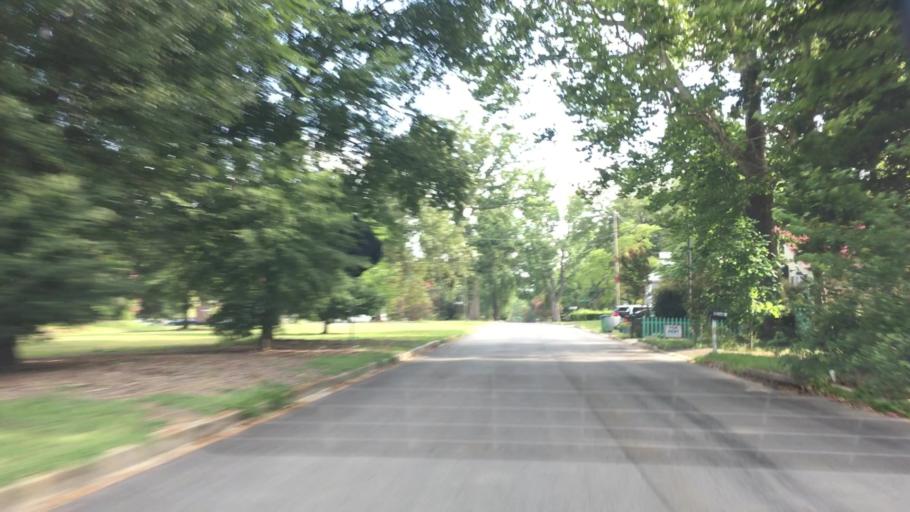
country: US
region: South Carolina
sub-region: Aiken County
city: Aiken
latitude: 33.5653
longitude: -81.7172
